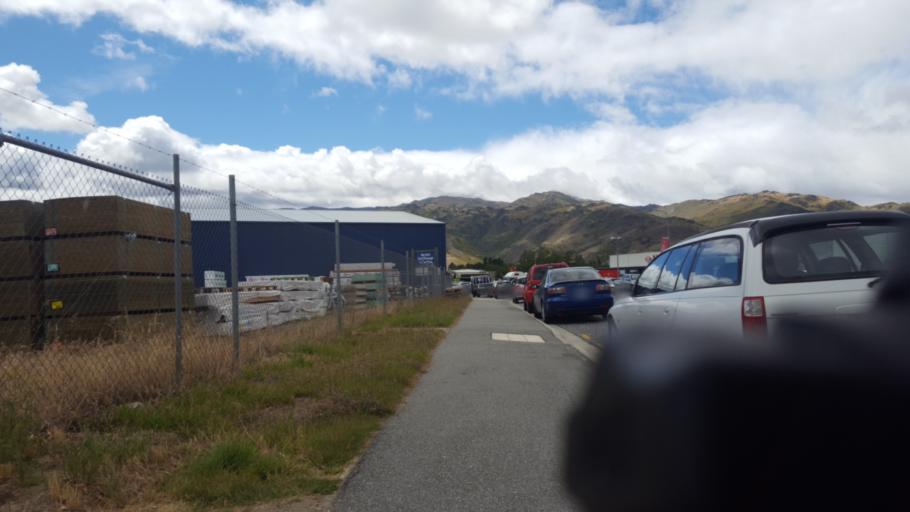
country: NZ
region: Otago
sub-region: Queenstown-Lakes District
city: Wanaka
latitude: -45.0372
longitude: 169.1934
